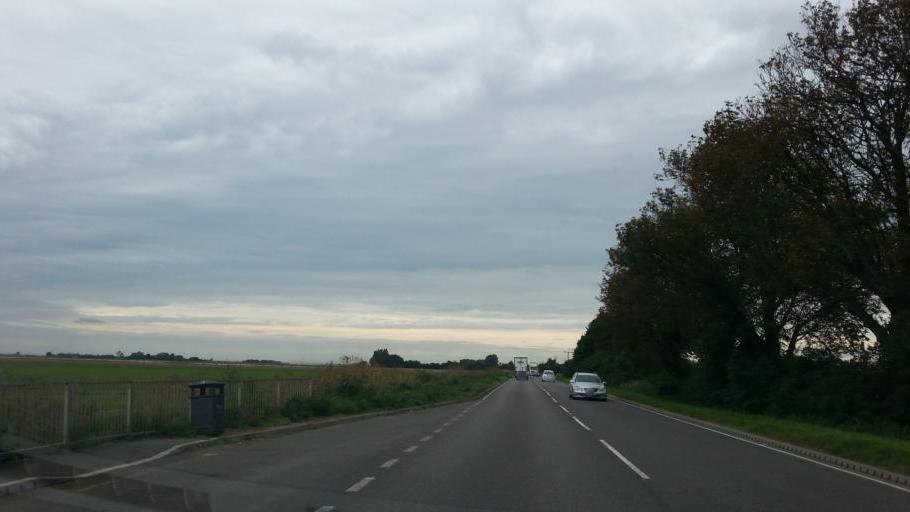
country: GB
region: England
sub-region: Cambridgeshire
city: March
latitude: 52.6107
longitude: 0.0302
